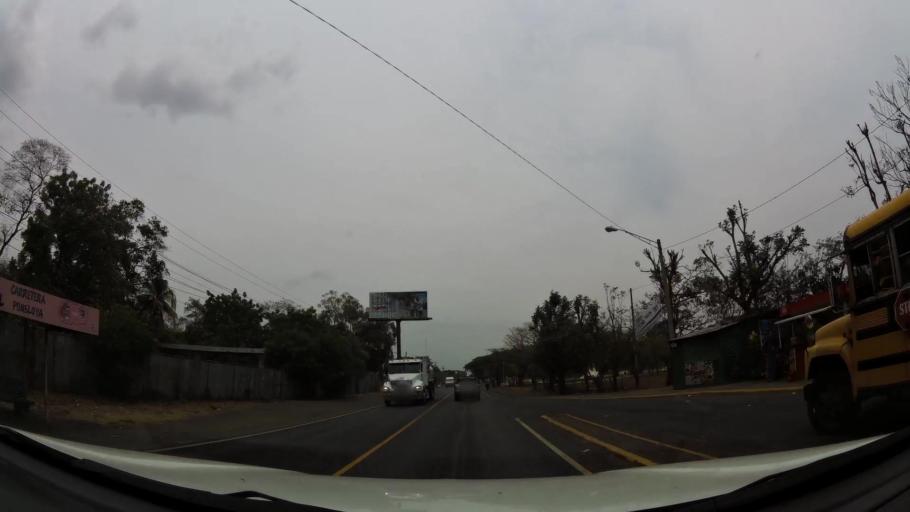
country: NI
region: Leon
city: Leon
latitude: 12.4192
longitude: -86.8704
